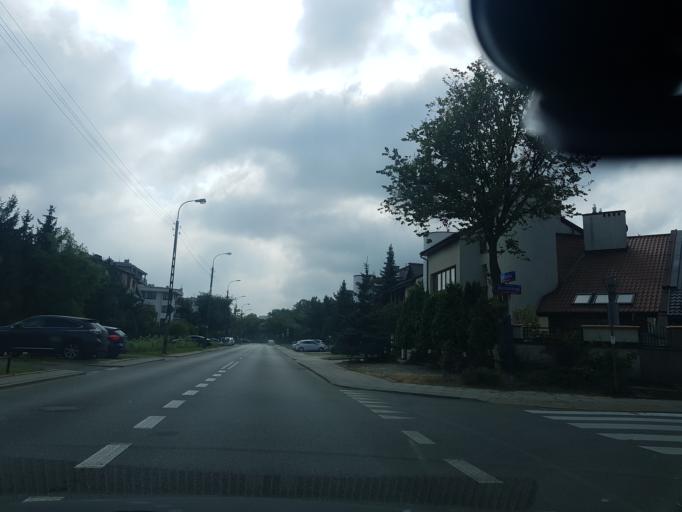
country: PL
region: Masovian Voivodeship
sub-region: Warszawa
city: Zoliborz
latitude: 52.2805
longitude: 20.9673
